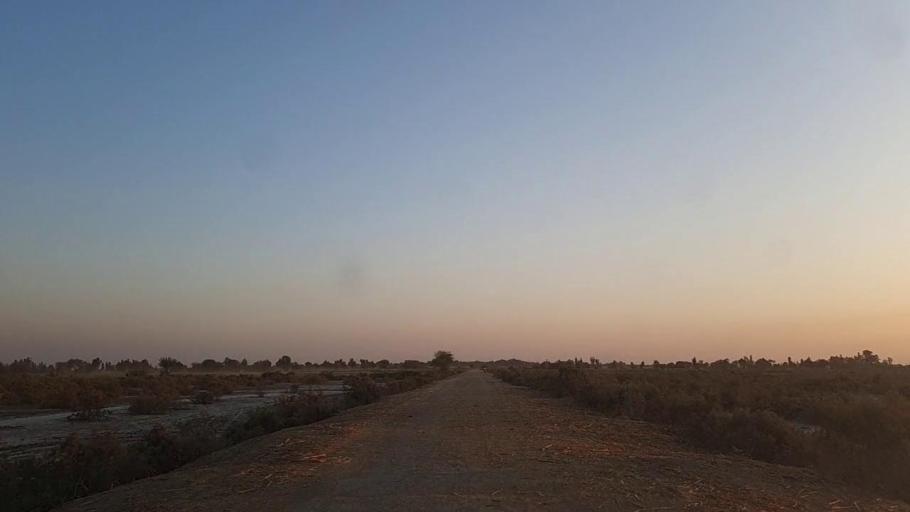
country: PK
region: Sindh
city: Samaro
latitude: 25.3180
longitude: 69.3691
